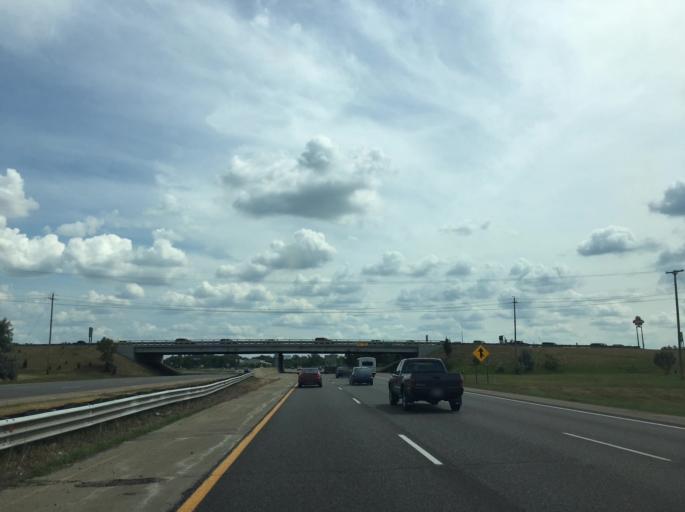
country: US
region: Michigan
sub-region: Genesee County
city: Beecher
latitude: 43.0621
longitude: -83.7627
